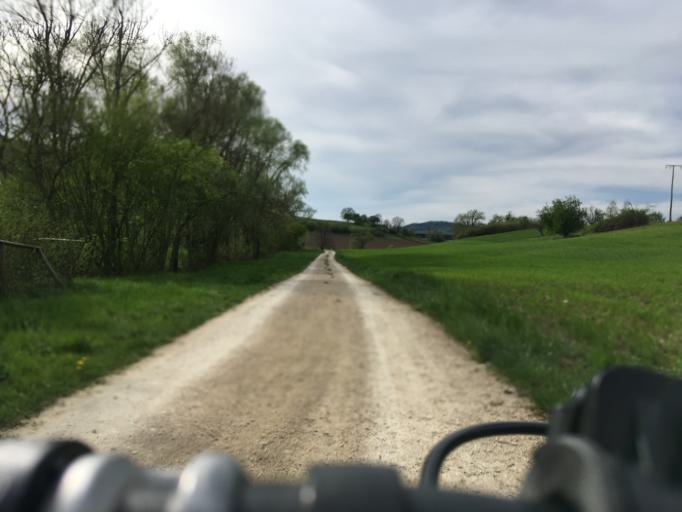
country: DE
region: Baden-Wuerttemberg
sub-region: Freiburg Region
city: Hilzingen
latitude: 47.7525
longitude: 8.7942
